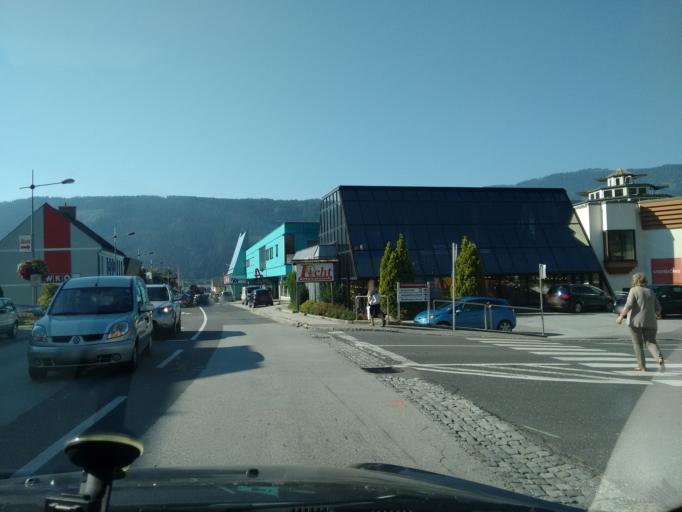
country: AT
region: Styria
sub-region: Politischer Bezirk Liezen
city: Liezen
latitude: 47.5655
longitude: 14.2439
